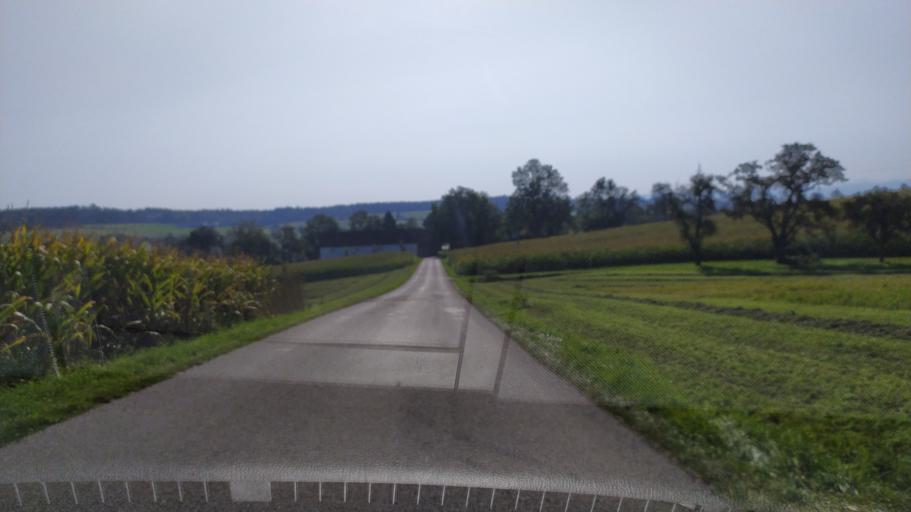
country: AT
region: Lower Austria
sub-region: Politischer Bezirk Amstetten
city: Zeillern
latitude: 48.1102
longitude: 14.7440
